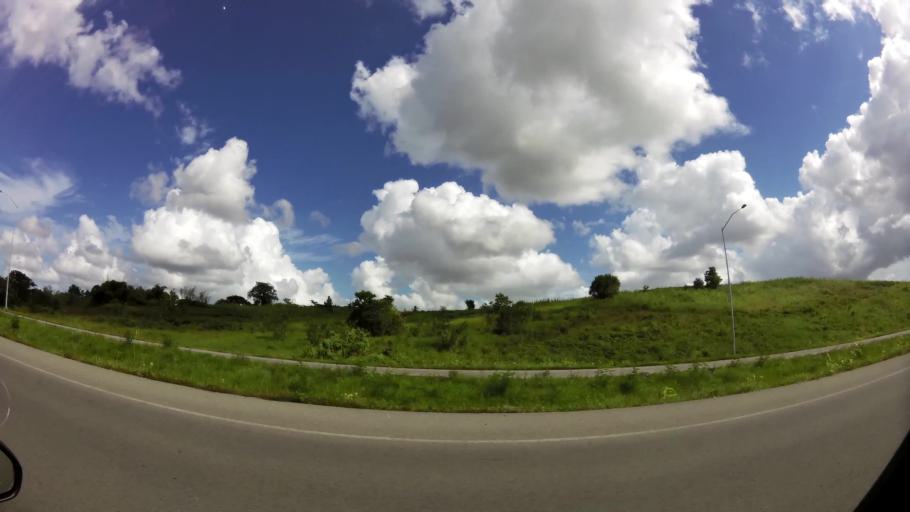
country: TT
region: Penal/Debe
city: Debe
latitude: 10.2333
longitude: -61.4475
